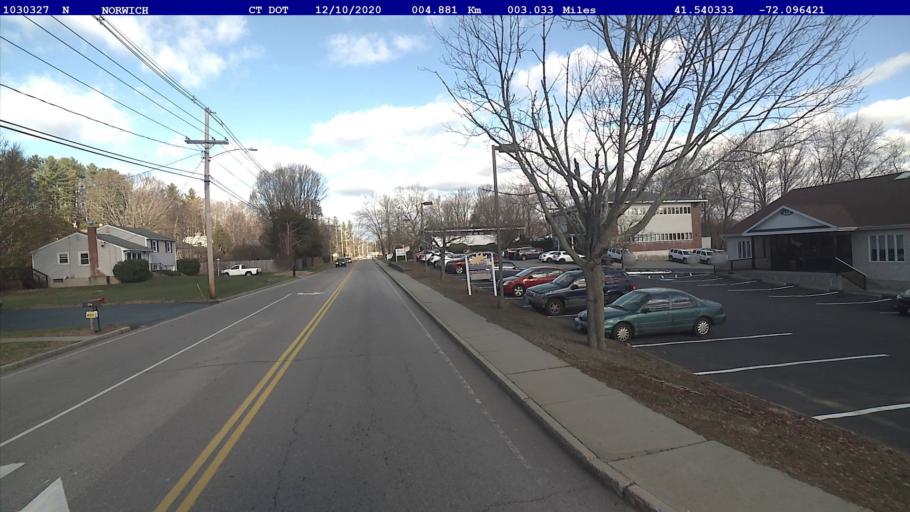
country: US
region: Connecticut
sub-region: New London County
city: Norwich
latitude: 41.5403
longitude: -72.0964
